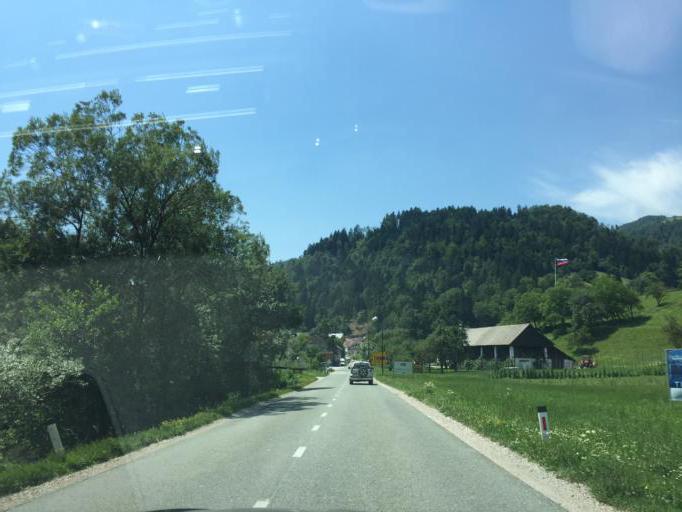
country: SI
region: Gorenja Vas-Poljane
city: Gorenja Vas
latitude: 46.1076
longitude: 14.1216
